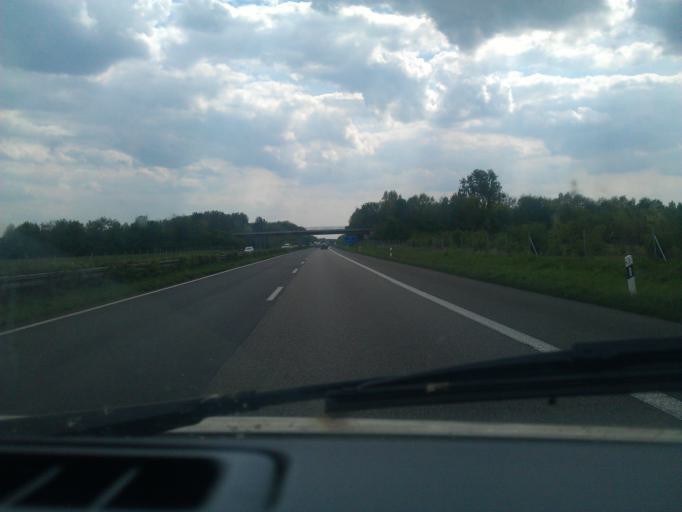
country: DE
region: North Rhine-Westphalia
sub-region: Regierungsbezirk Munster
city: Heek
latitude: 52.1839
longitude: 7.1107
